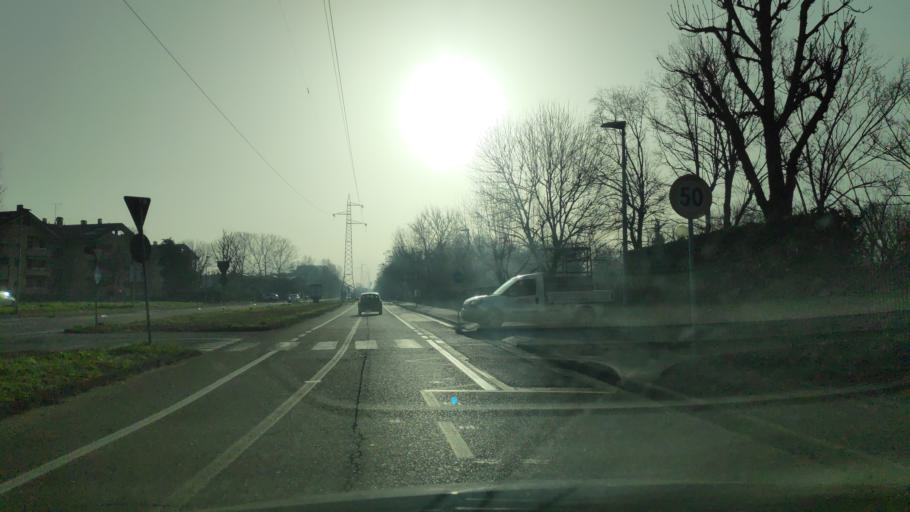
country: IT
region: Lombardy
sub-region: Citta metropolitana di Milano
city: Rozzano
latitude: 45.3927
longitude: 9.1592
